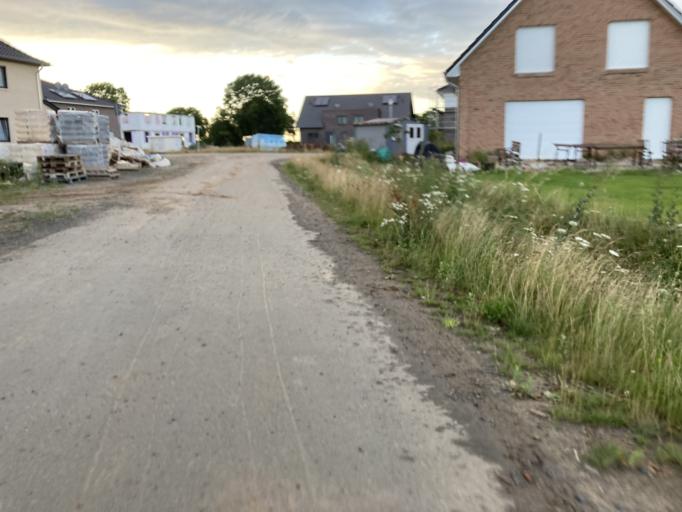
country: DE
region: Lower Saxony
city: Verden
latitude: 52.9263
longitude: 9.2084
